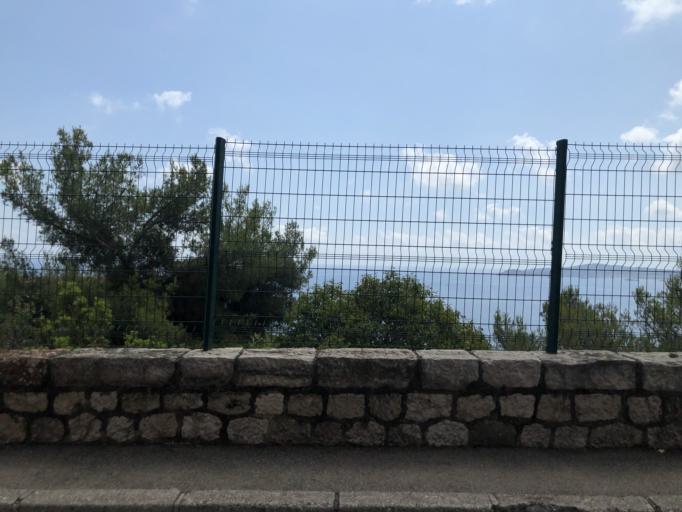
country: FR
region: Provence-Alpes-Cote d'Azur
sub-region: Departement des Alpes-Maritimes
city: Cap-d'Ail
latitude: 43.7236
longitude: 7.3917
